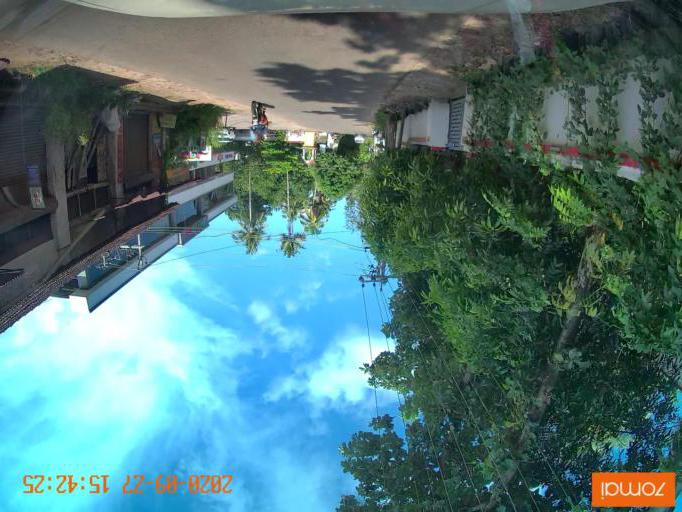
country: IN
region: Kerala
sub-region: Thrissur District
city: Thanniyam
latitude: 10.4728
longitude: 76.1023
